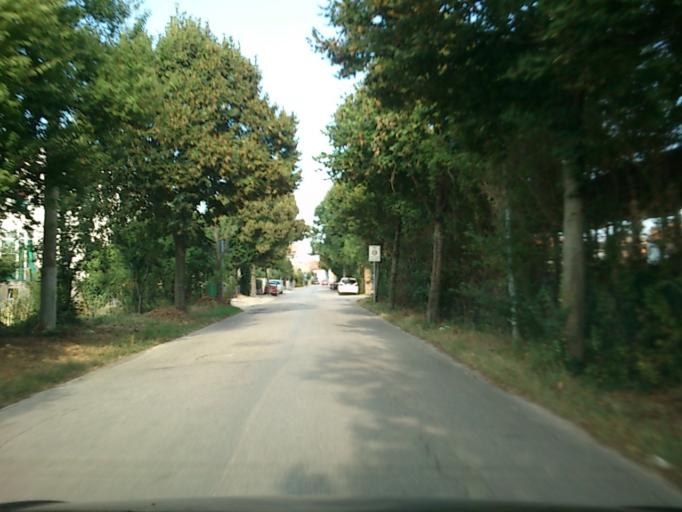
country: IT
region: The Marches
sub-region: Provincia di Pesaro e Urbino
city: Centinarola
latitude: 43.8314
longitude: 12.9972
